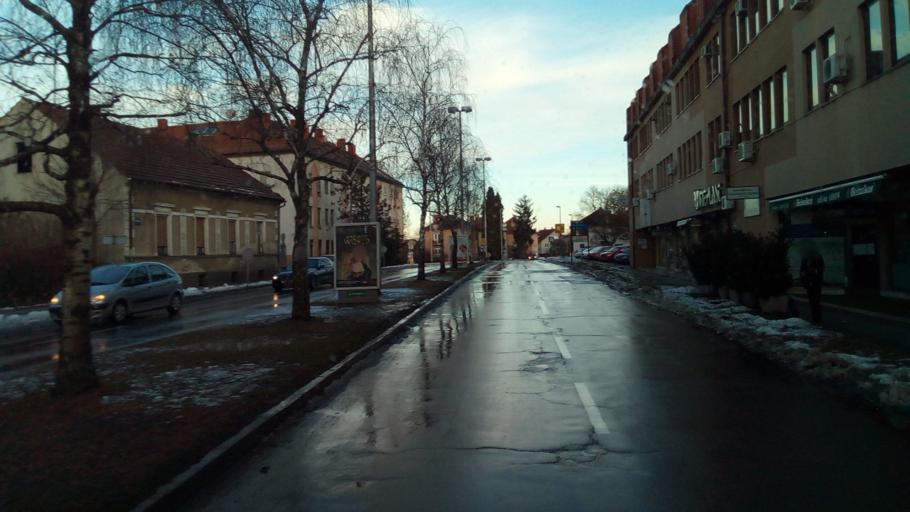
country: HR
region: Medimurska
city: Cakovec
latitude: 46.3900
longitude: 16.4404
